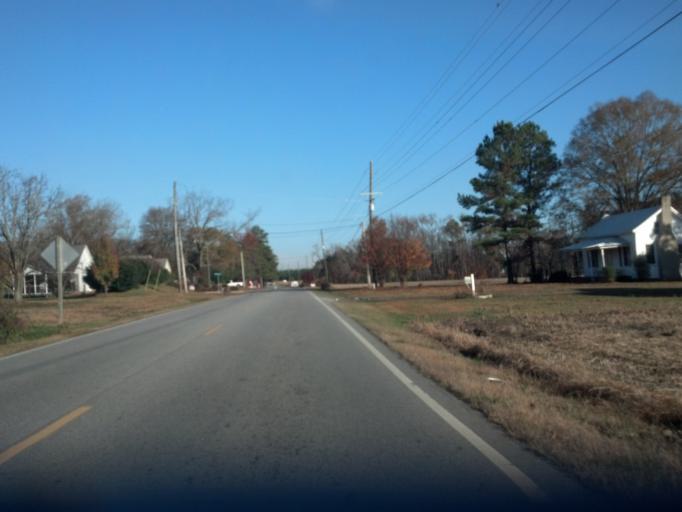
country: US
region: North Carolina
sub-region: Pitt County
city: Winterville
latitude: 35.5448
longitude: -77.4432
